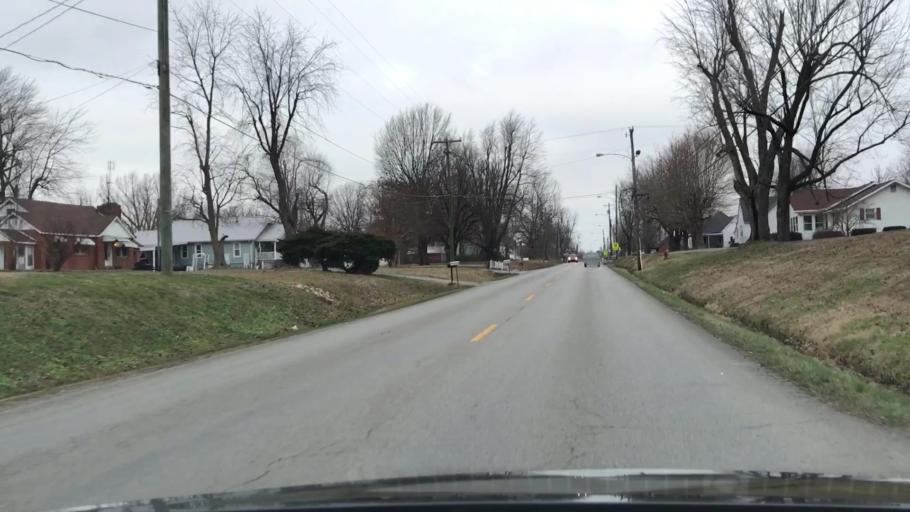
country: US
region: Kentucky
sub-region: McLean County
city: Calhoun
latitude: 37.4112
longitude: -87.2641
